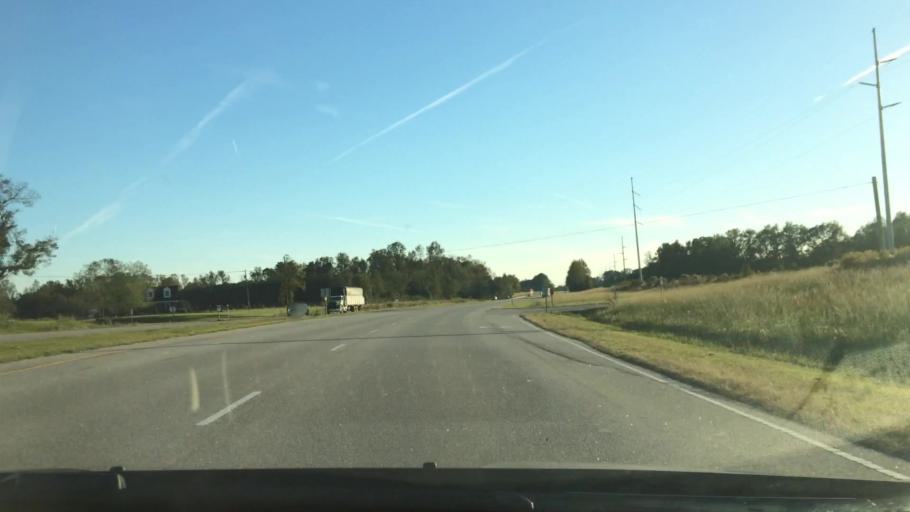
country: US
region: North Carolina
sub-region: Pitt County
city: Grifton
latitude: 35.4031
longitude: -77.4371
